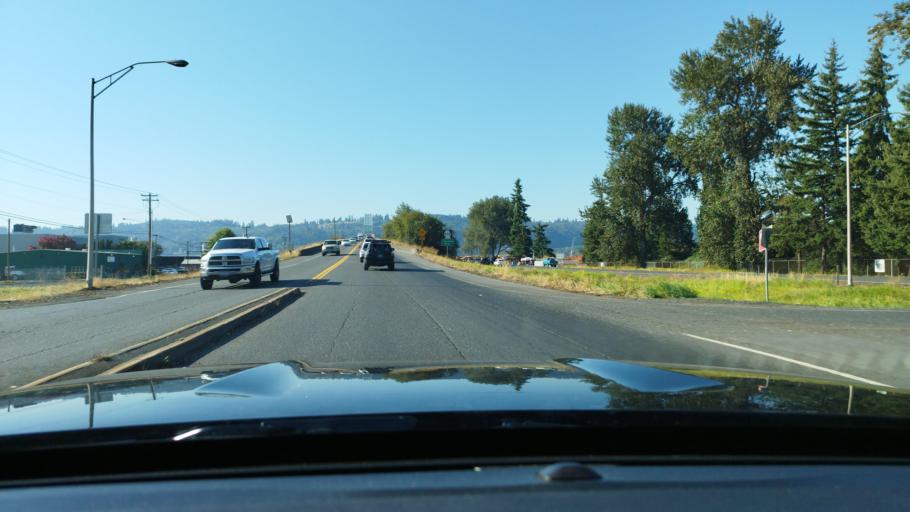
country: US
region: Washington
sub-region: Cowlitz County
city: Longview
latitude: 46.1151
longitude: -122.9528
